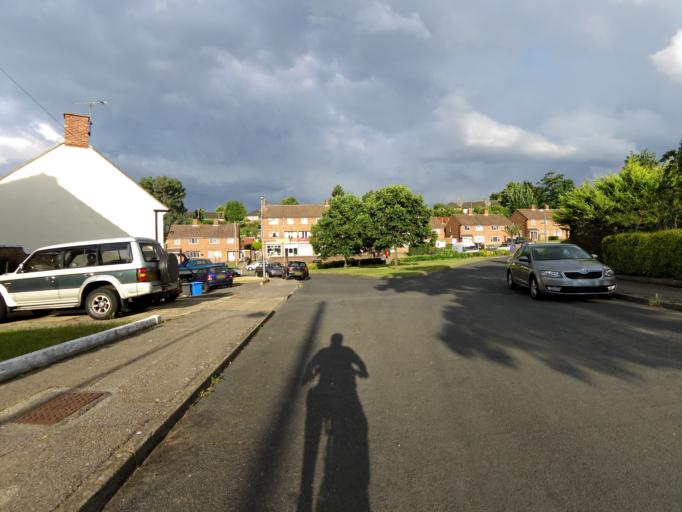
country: GB
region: England
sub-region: Suffolk
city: Ipswich
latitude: 52.0501
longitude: 1.1277
